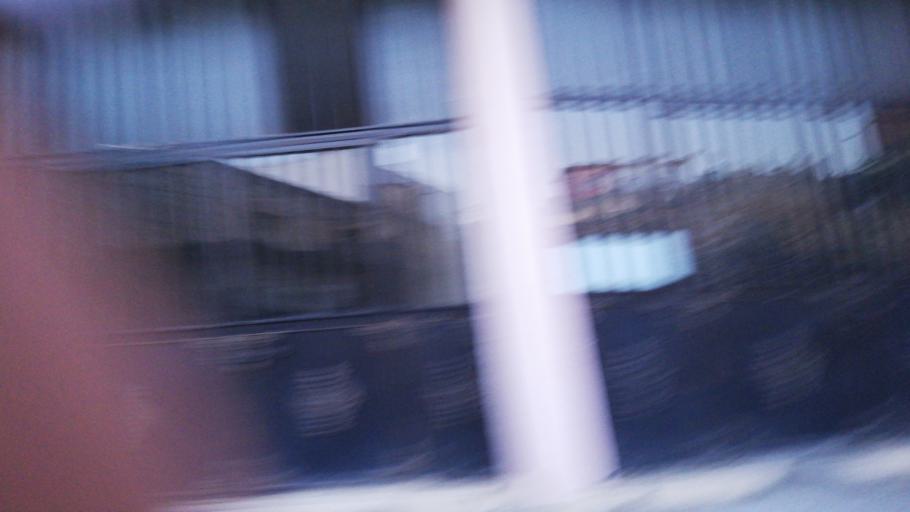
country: TR
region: Mardin
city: Kindirip
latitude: 37.4473
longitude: 41.2195
